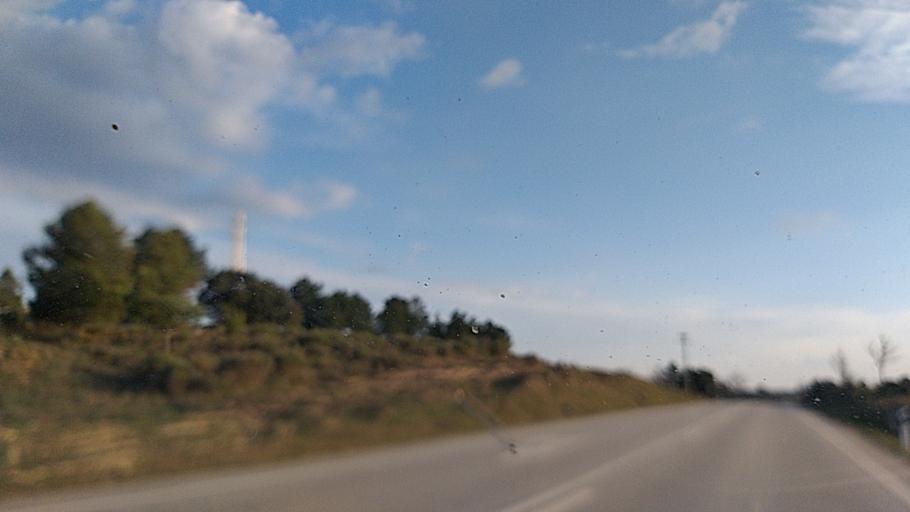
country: ES
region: Castille and Leon
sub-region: Provincia de Salamanca
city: Fuentes de Onoro
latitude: 40.6325
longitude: -6.9731
